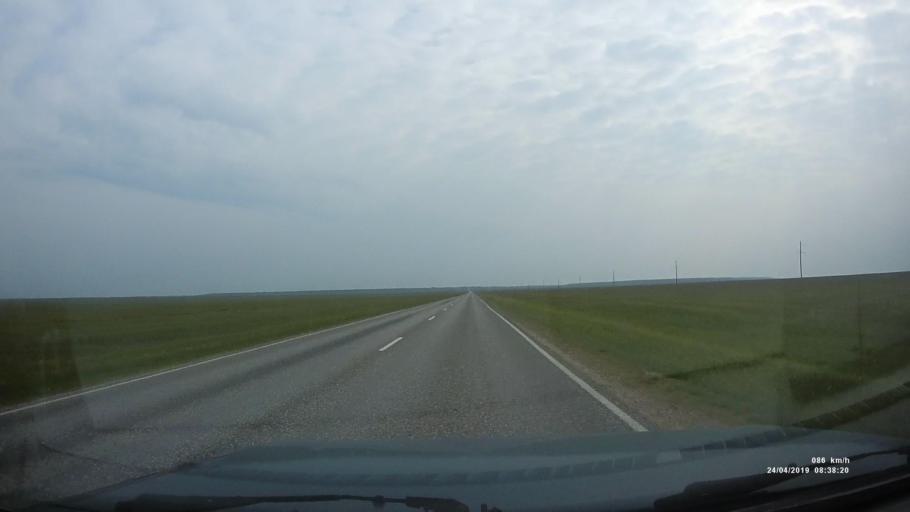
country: RU
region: Kalmykiya
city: Arshan'
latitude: 46.2148
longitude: 43.9657
